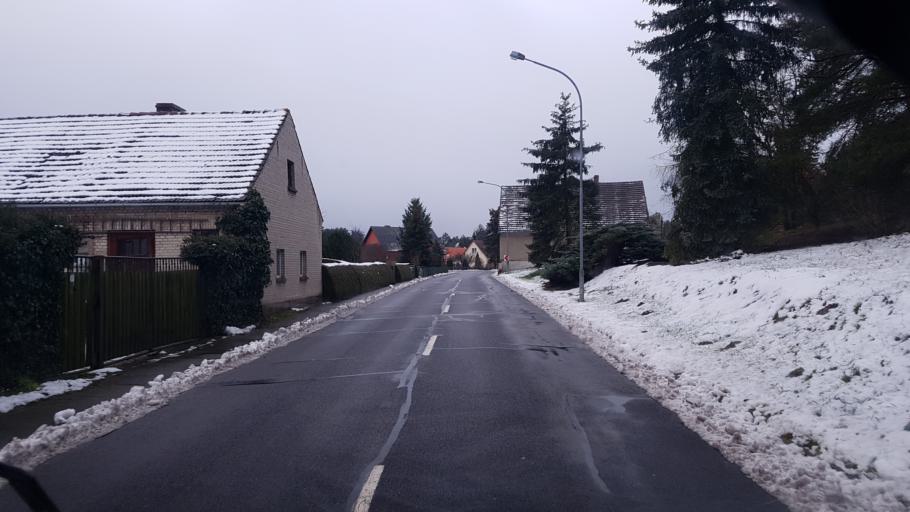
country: DE
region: Brandenburg
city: Schenkendobern
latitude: 51.9334
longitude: 14.6219
